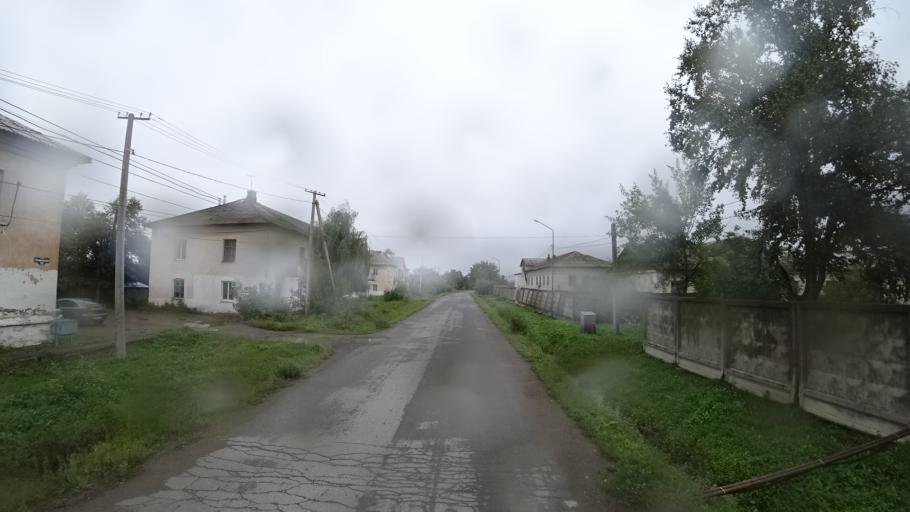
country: RU
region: Primorskiy
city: Monastyrishche
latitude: 44.1978
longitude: 132.4296
